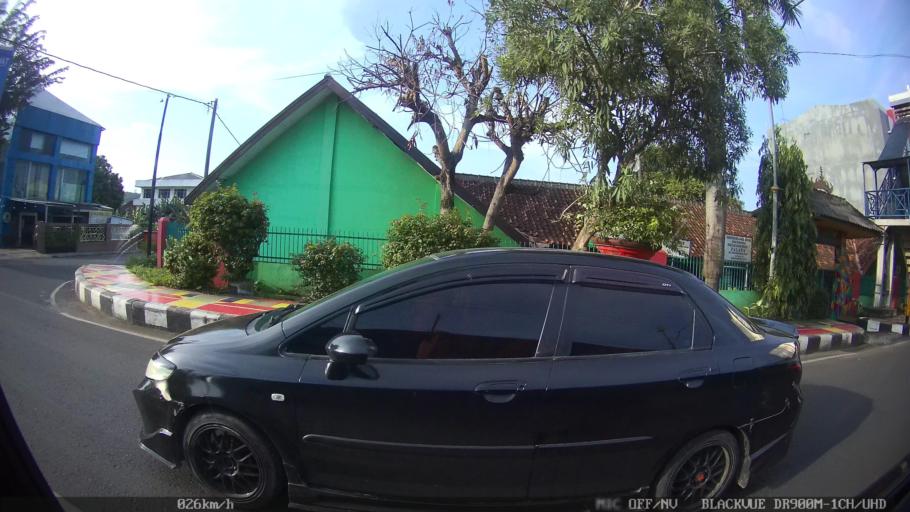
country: ID
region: Lampung
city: Bandarlampung
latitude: -5.4216
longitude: 105.2544
